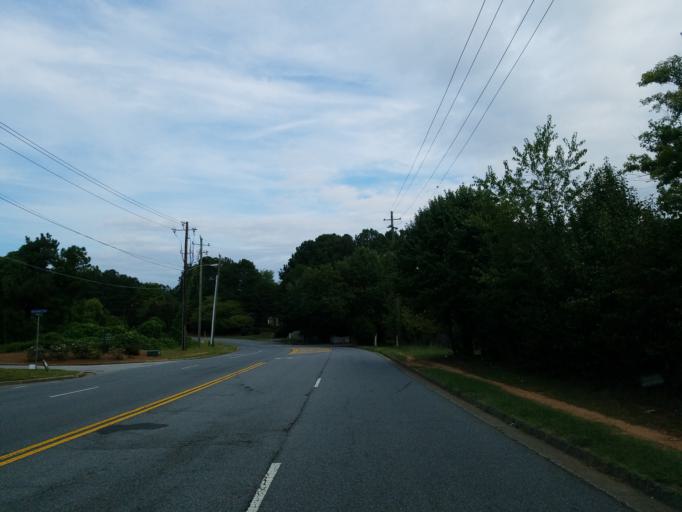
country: US
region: Georgia
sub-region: Cobb County
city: Marietta
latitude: 33.9936
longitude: -84.5482
